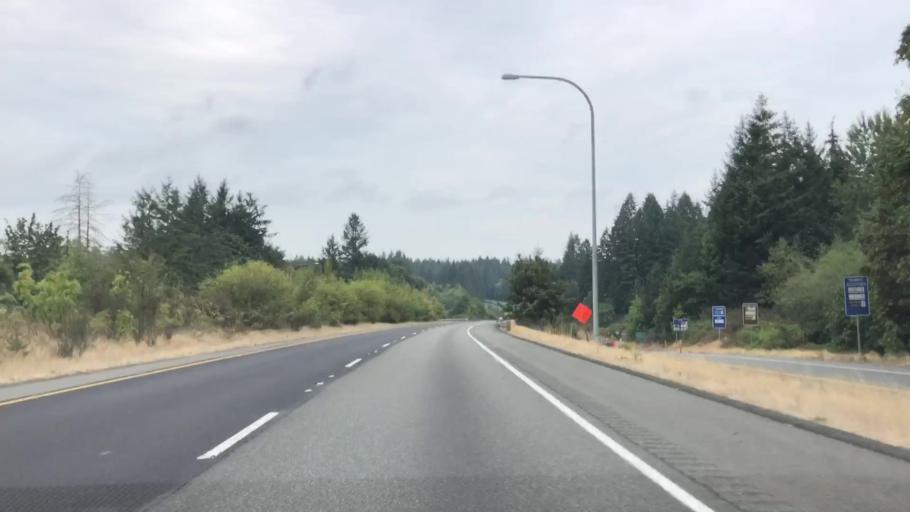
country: US
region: Washington
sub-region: Kitsap County
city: Port Orchard
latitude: 47.5194
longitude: -122.6592
